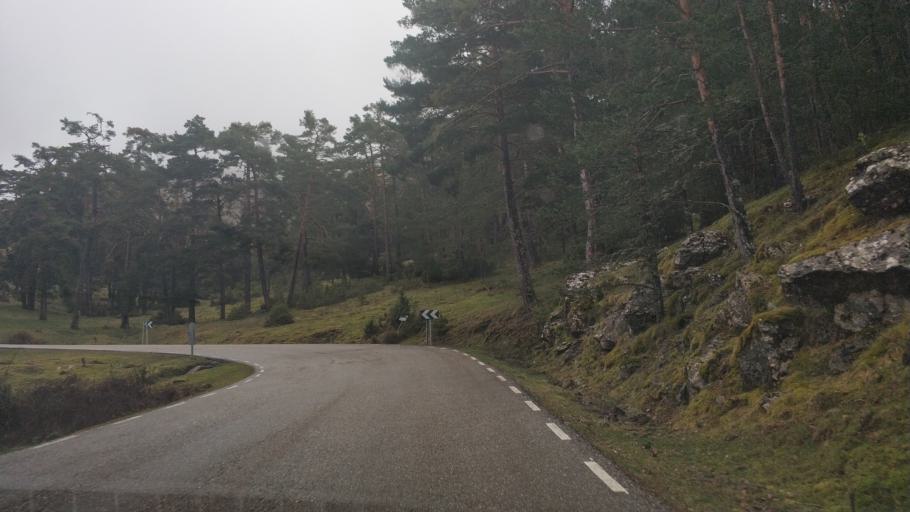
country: ES
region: Castille and Leon
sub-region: Provincia de Burgos
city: Neila
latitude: 42.0312
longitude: -3.0060
